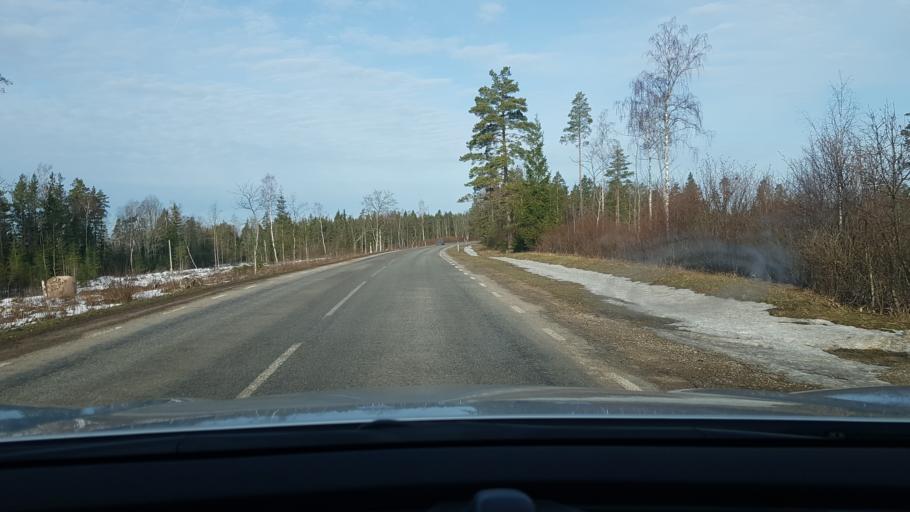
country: EE
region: Saare
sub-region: Kuressaare linn
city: Kuressaare
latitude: 58.4609
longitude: 22.7045
